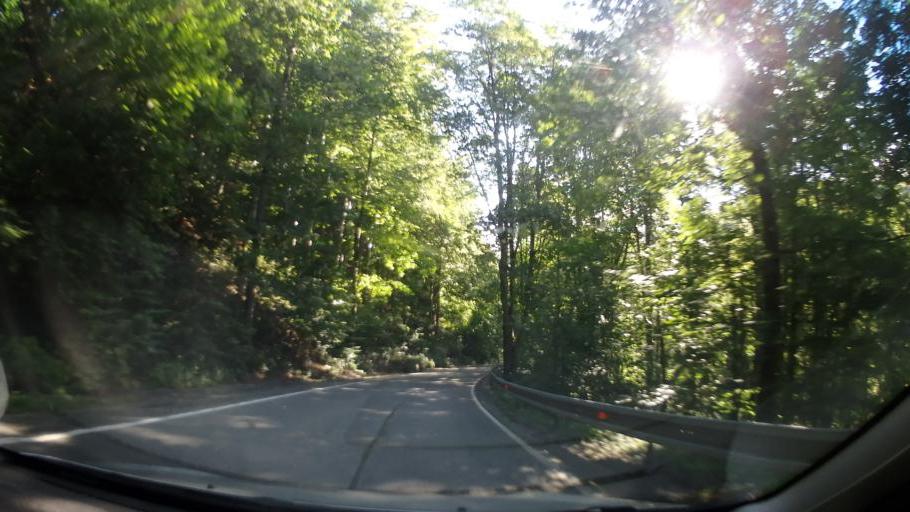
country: CZ
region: Olomoucky
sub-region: Okres Jesenik
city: Jesenik
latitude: 50.2063
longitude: 17.2408
